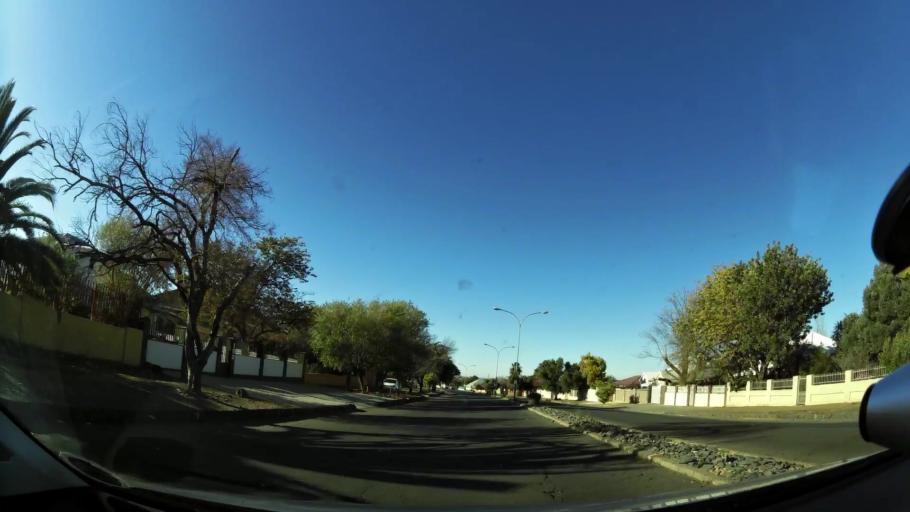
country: ZA
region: Northern Cape
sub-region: Frances Baard District Municipality
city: Kimberley
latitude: -28.7532
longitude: 24.7806
